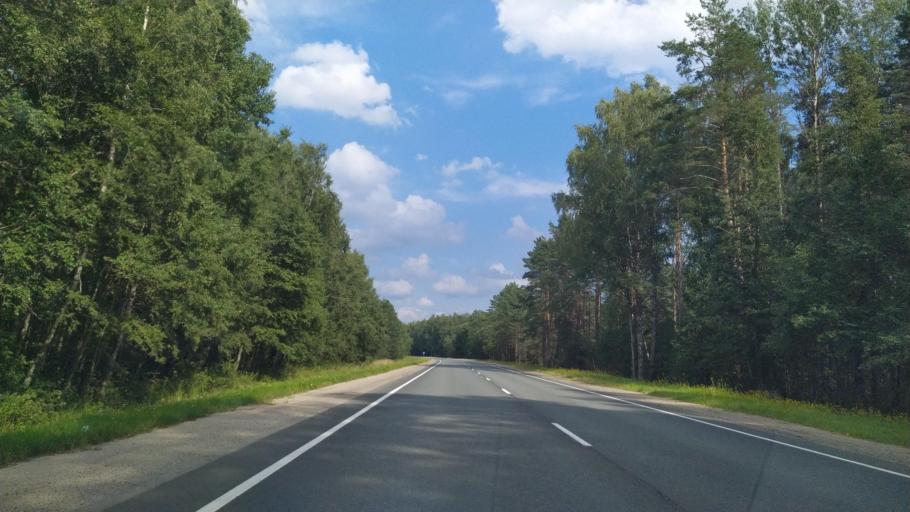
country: RU
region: Pskov
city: Porkhov
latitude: 57.8638
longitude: 29.5877
